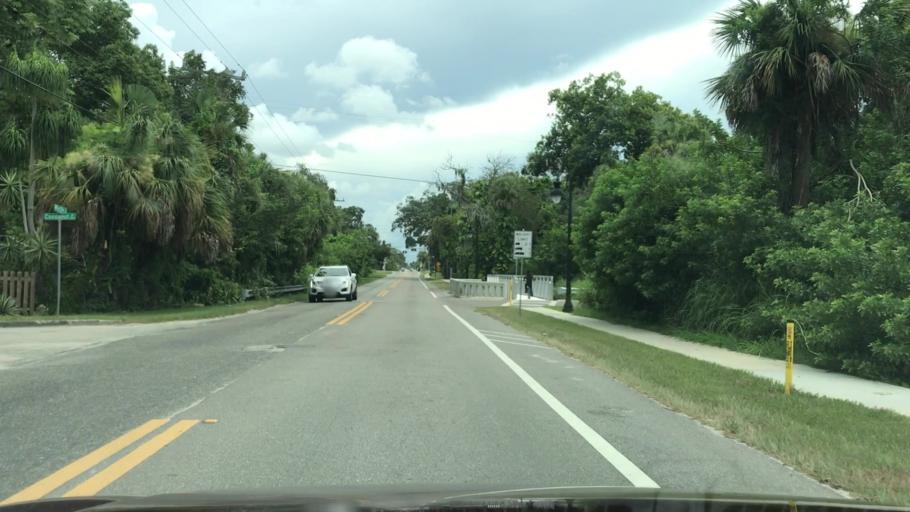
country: US
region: Florida
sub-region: Sarasota County
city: North Sarasota
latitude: 27.3672
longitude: -82.5450
